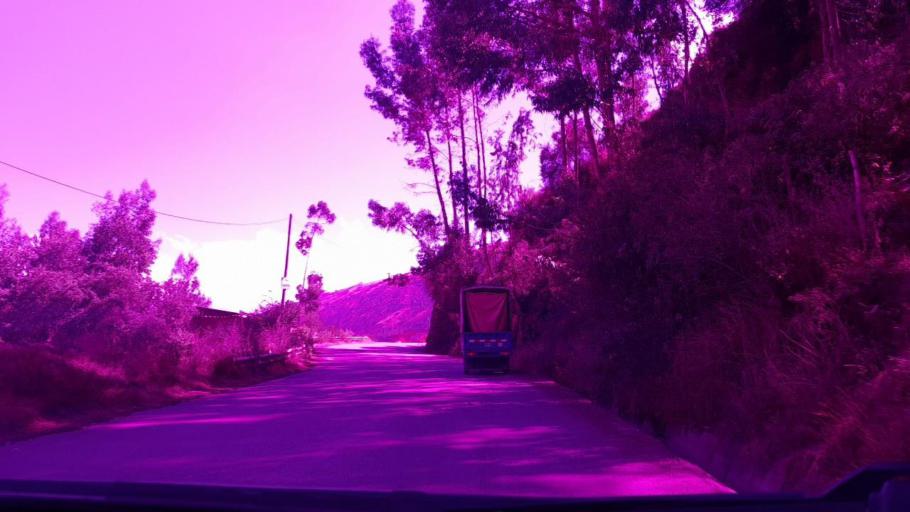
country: PE
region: Cusco
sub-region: Provincia de Cusco
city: Cusco
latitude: -13.5221
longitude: -71.9085
